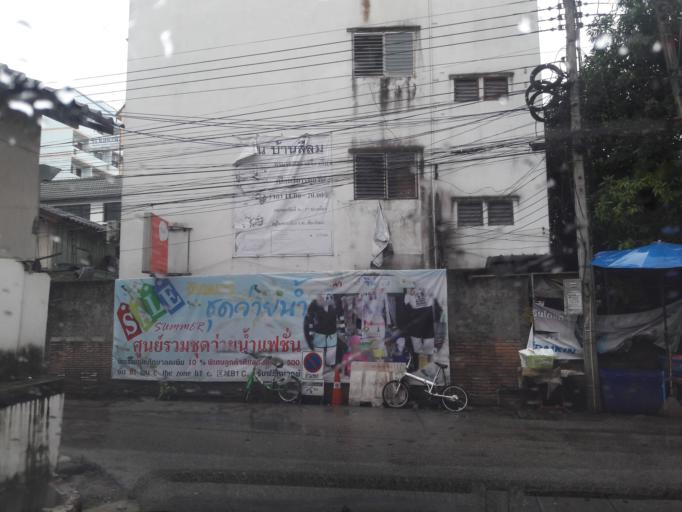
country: TH
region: Chiang Mai
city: Chiang Mai
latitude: 18.7946
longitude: 98.9762
